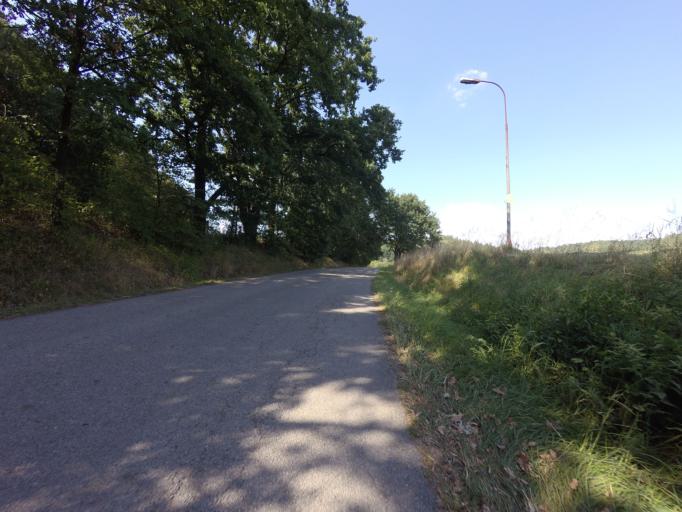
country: CZ
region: Jihocesky
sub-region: Okres Ceske Budejovice
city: Hluboka nad Vltavou
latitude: 49.1329
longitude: 14.4494
